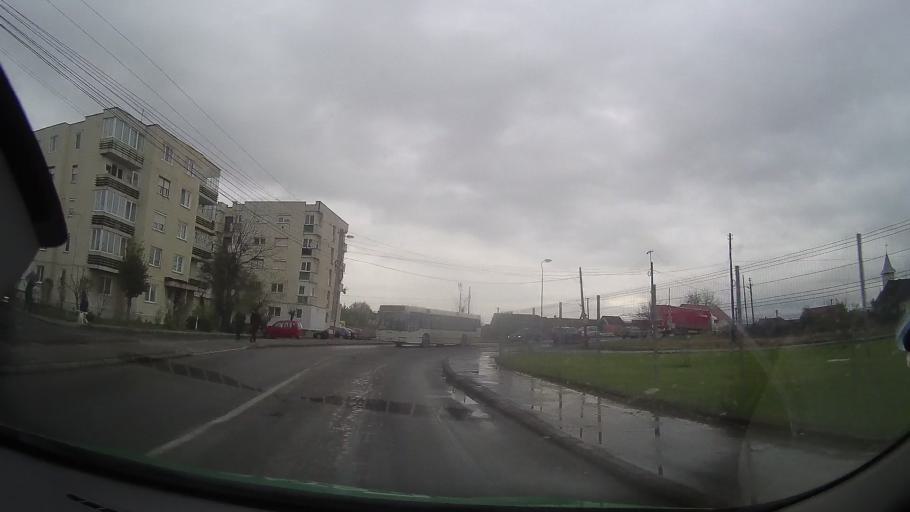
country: RO
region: Mures
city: Reghin-Sat
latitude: 46.7779
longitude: 24.7167
